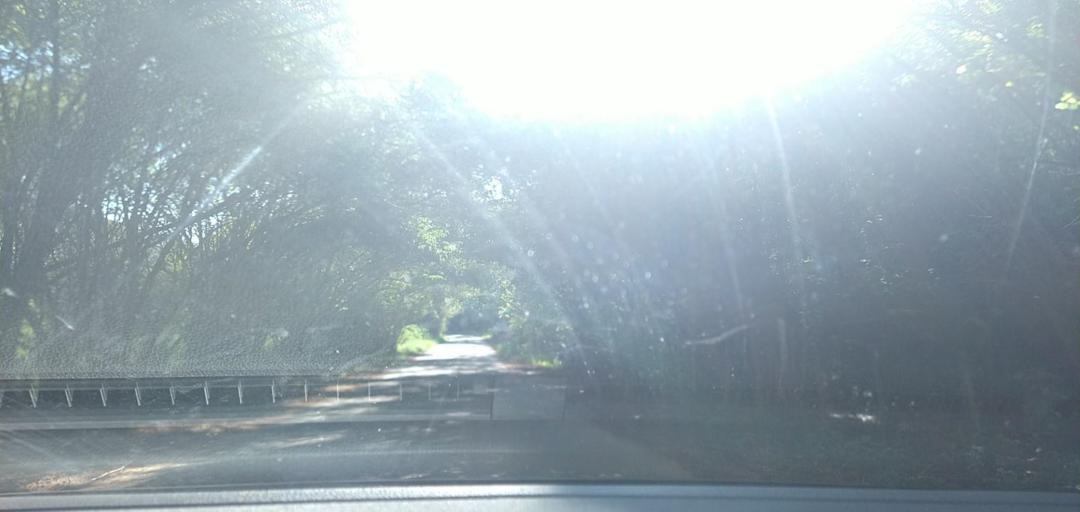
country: BR
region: Minas Gerais
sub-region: Alvinopolis
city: Alvinopolis
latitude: -20.1756
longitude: -42.9262
